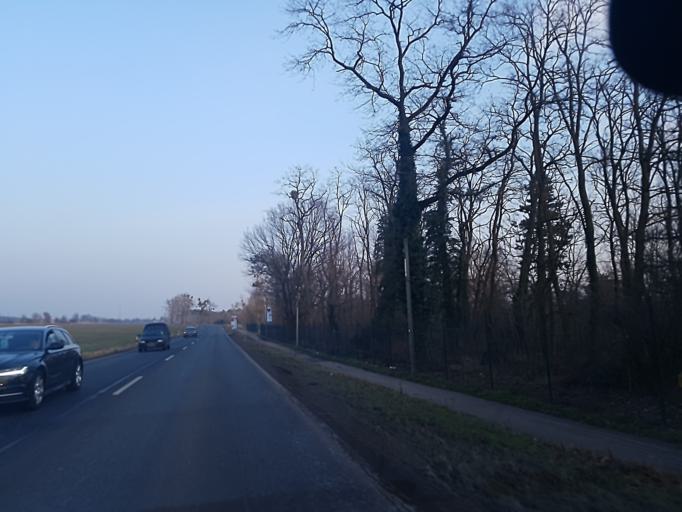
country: DE
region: Saxony-Anhalt
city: Coswig
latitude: 51.8791
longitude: 12.5254
